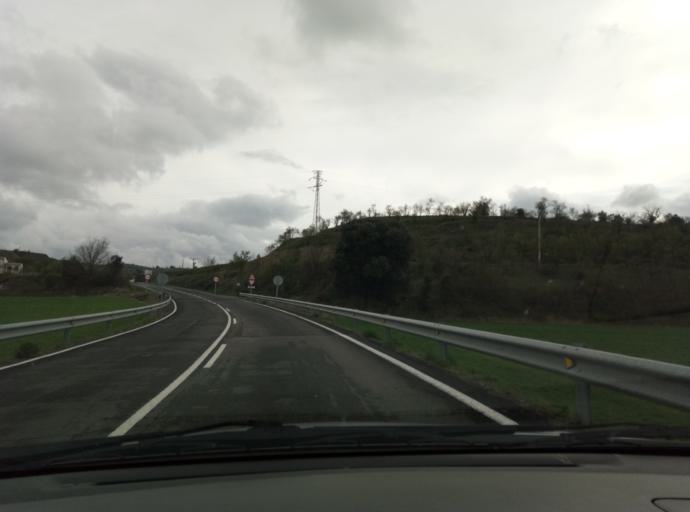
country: ES
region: Catalonia
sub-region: Provincia de Lleida
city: Cervera
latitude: 41.6280
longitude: 1.3397
